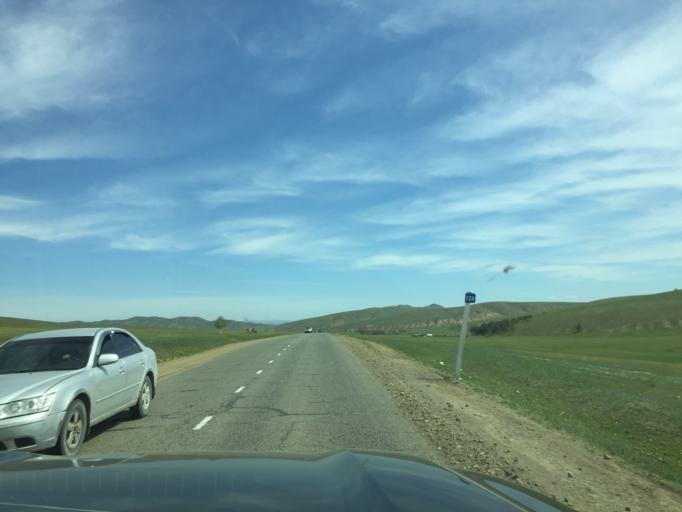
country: MN
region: Central Aimak
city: Javhlant
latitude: 48.6575
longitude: 106.1165
